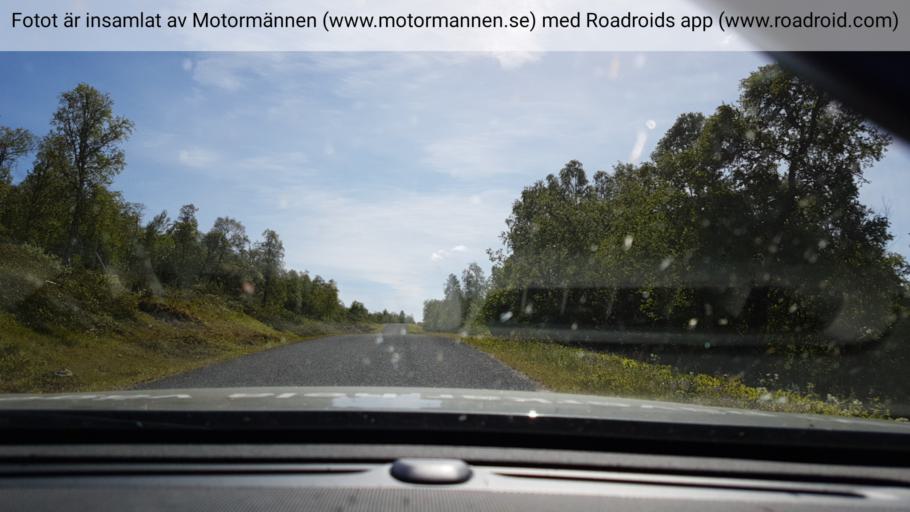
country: NO
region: Nordland
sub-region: Hattfjelldal
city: Hattfjelldal
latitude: 65.4220
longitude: 14.6718
